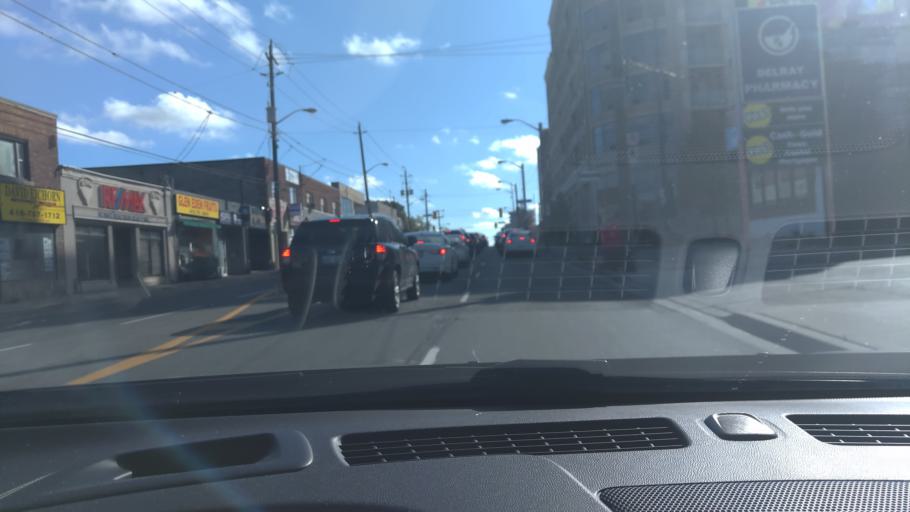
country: CA
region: Ontario
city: Toronto
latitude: 43.7135
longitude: -79.4287
